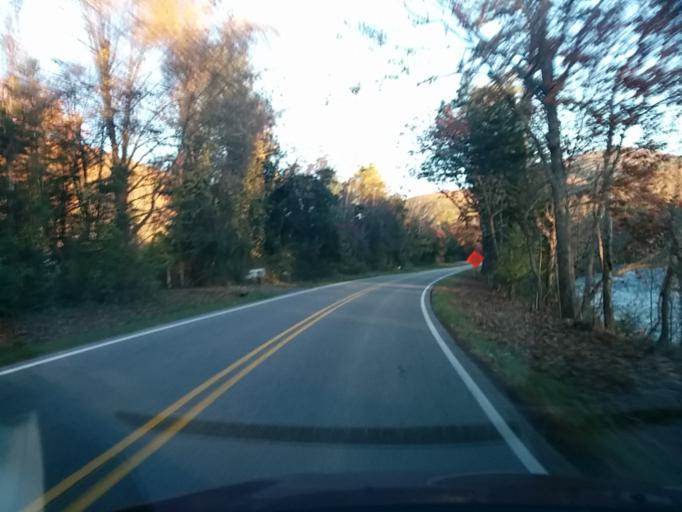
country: US
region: Virginia
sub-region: Rockbridge County
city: East Lexington
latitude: 37.9107
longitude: -79.4283
